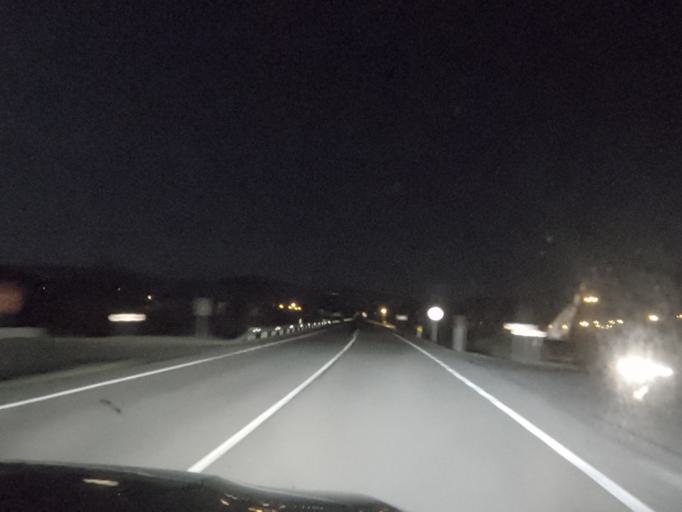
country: ES
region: Galicia
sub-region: Provincia de Ourense
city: Verin
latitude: 41.9544
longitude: -7.4991
